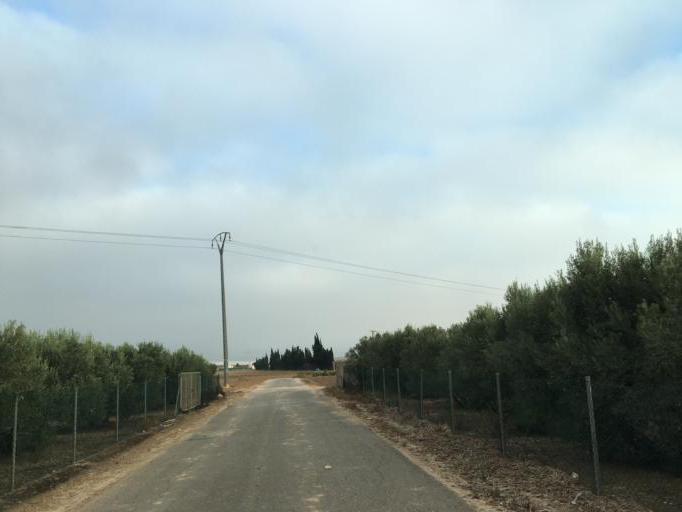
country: ES
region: Murcia
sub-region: Murcia
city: La Union
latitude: 37.6656
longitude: -0.9368
